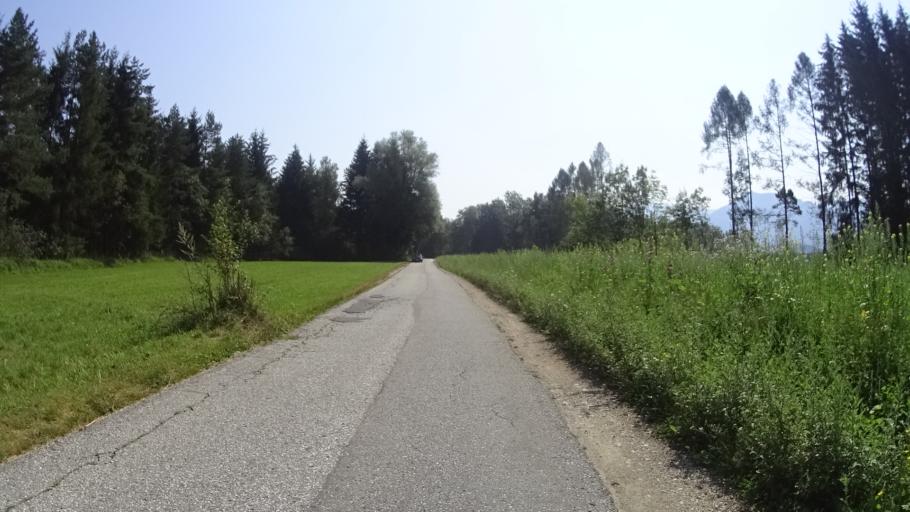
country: AT
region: Carinthia
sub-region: Politischer Bezirk Volkermarkt
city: Gallizien
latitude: 46.5612
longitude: 14.5493
